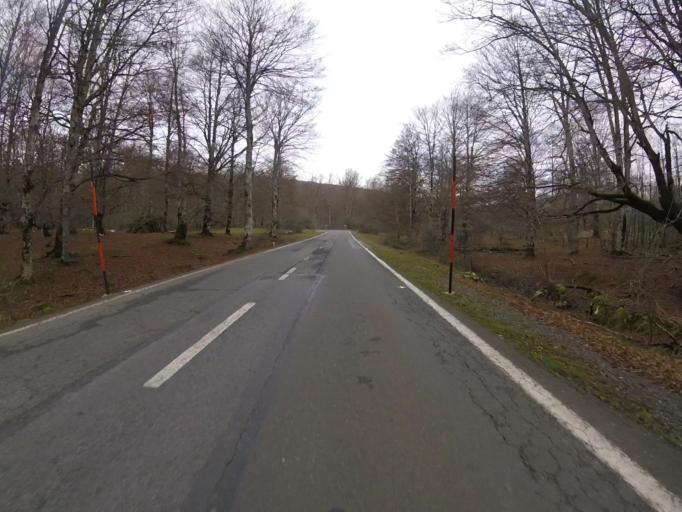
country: ES
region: Navarre
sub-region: Provincia de Navarra
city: Olazagutia
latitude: 42.8552
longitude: -2.1699
